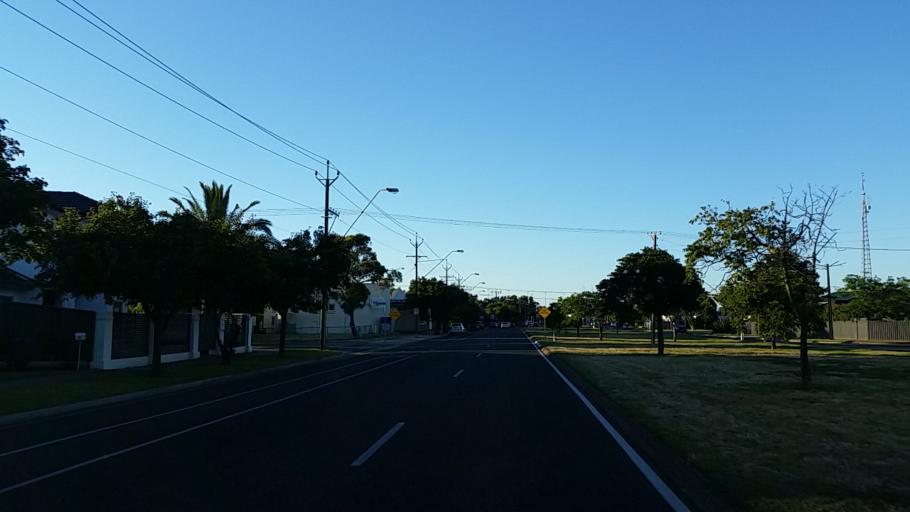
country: AU
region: South Australia
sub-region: City of West Torrens
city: Plympton
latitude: -34.9291
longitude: 138.5427
